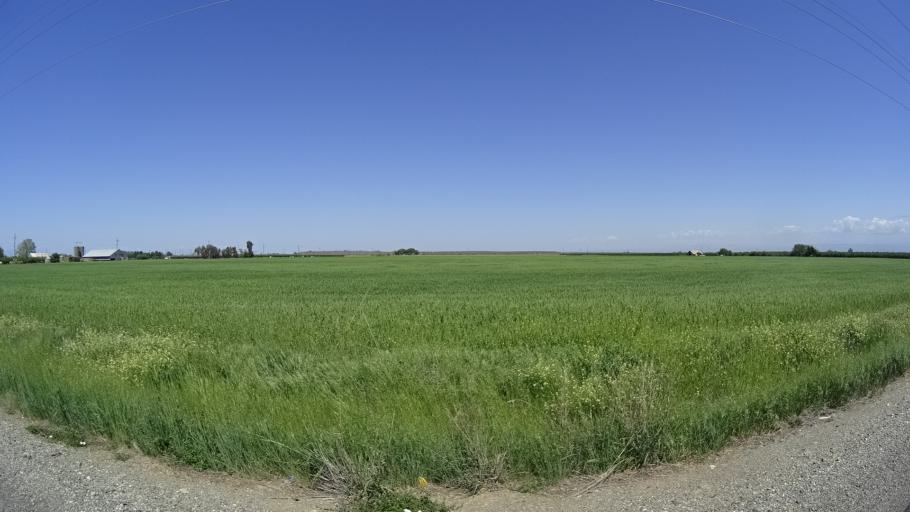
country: US
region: California
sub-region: Glenn County
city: Orland
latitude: 39.7685
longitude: -122.1360
